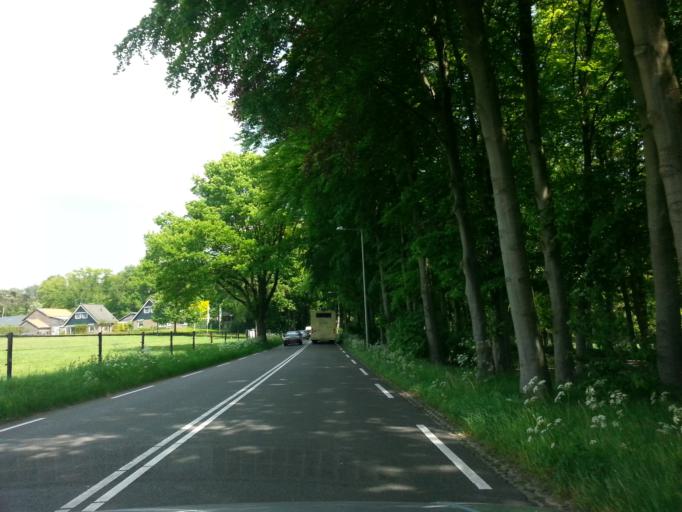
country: NL
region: Gelderland
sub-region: Gemeente Arnhem
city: Gulden Bodem
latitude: 52.0041
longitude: 5.8892
